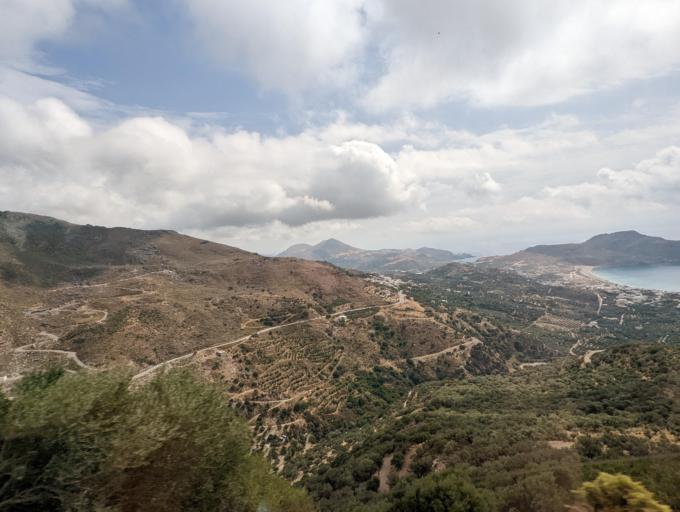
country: GR
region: Crete
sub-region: Nomos Rethymnis
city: Atsipopoulon
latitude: 35.2090
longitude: 24.3930
